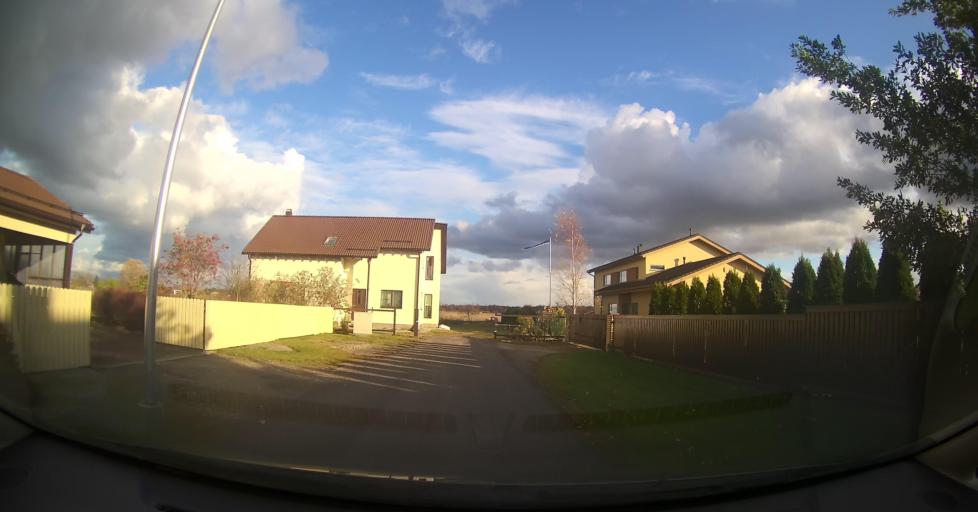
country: EE
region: Harju
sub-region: Joelaehtme vald
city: Loo
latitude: 59.4414
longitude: 24.9635
